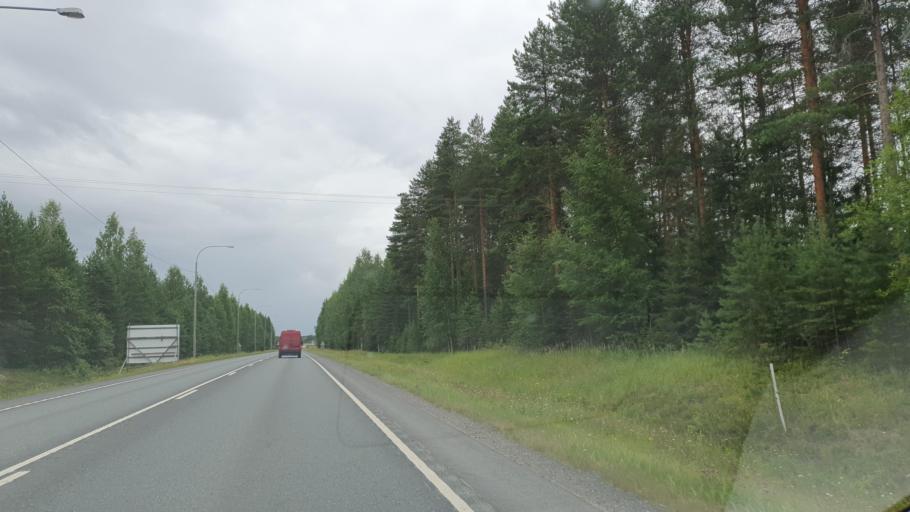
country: FI
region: Northern Savo
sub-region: Ylae-Savo
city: Lapinlahti
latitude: 63.2678
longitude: 27.4648
